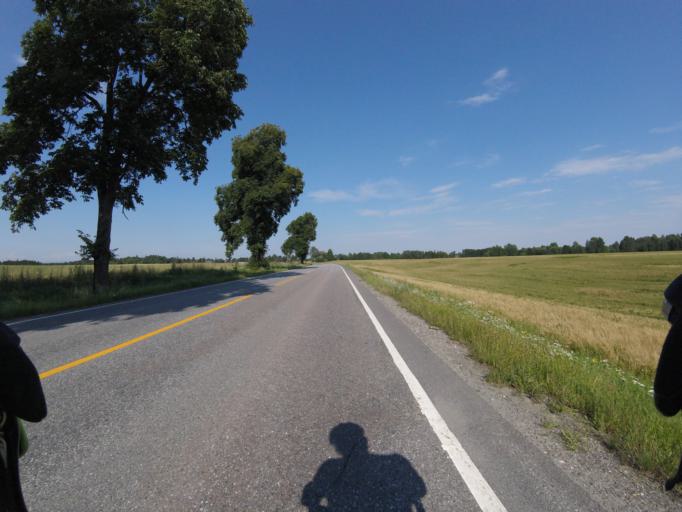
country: NO
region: Akershus
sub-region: Ullensaker
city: Klofta
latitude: 60.0589
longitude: 11.1204
